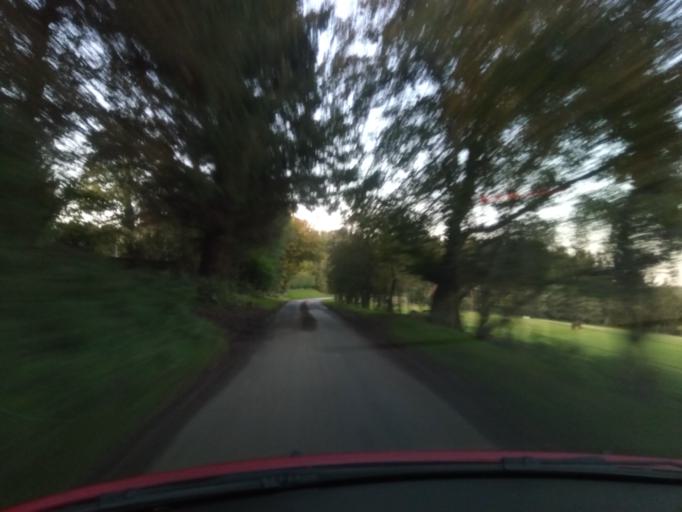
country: GB
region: Scotland
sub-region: Fife
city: Pathhead
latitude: 55.7944
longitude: -2.8895
